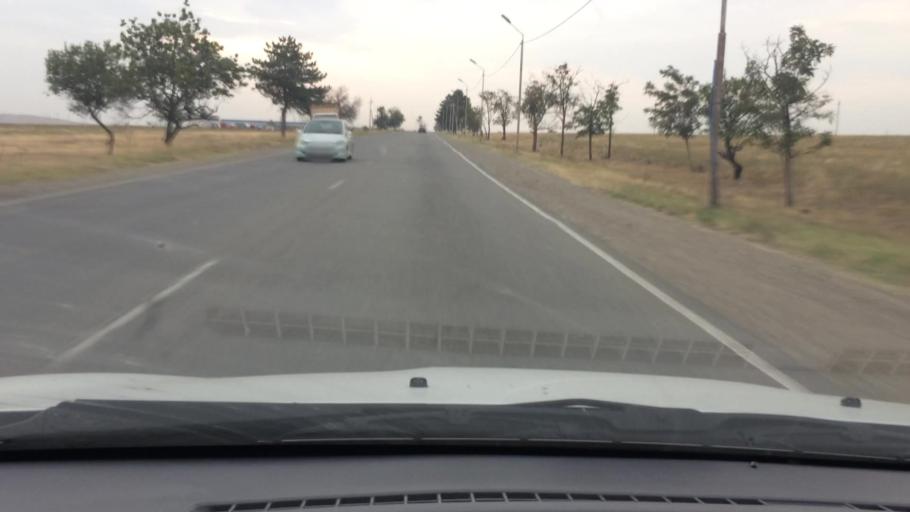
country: GE
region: Kvemo Kartli
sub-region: Marneuli
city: Marneuli
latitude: 41.5158
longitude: 44.7854
